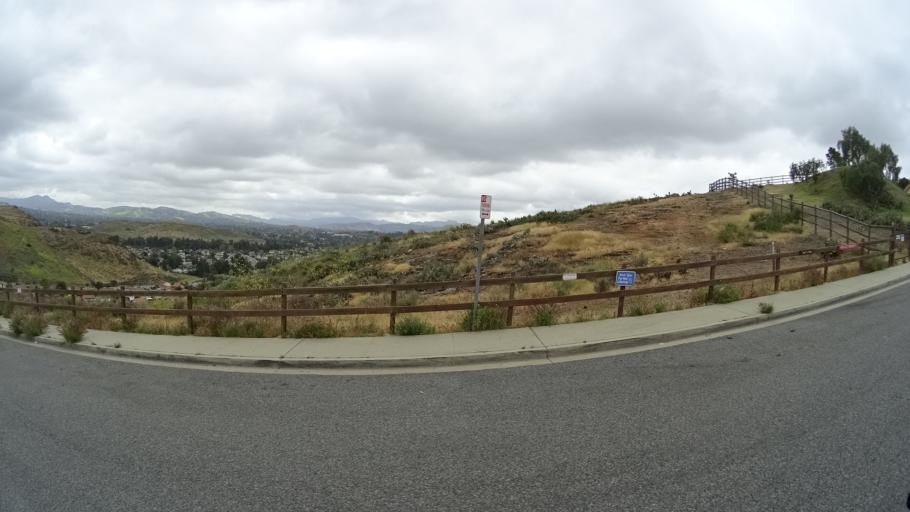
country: US
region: California
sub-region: Ventura County
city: Moorpark
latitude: 34.2273
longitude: -118.8986
